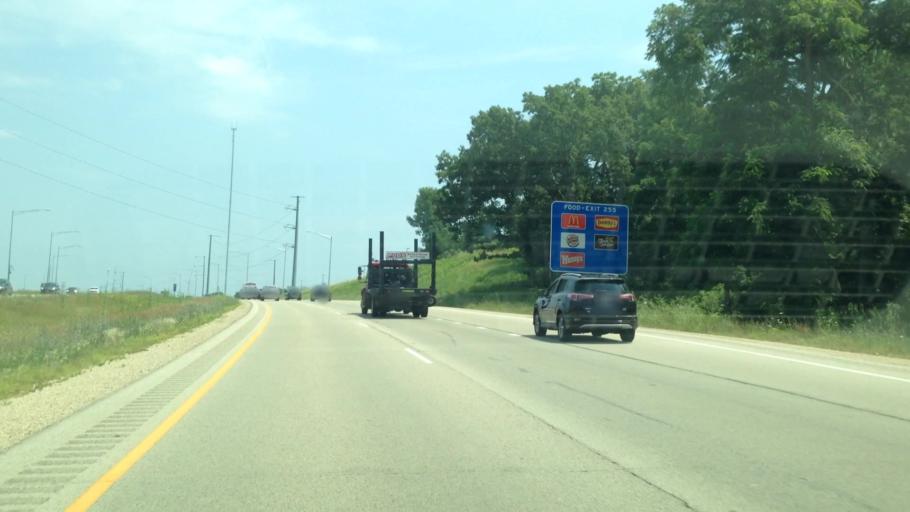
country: US
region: Wisconsin
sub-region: Dane County
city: Middleton
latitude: 43.0533
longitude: -89.5122
